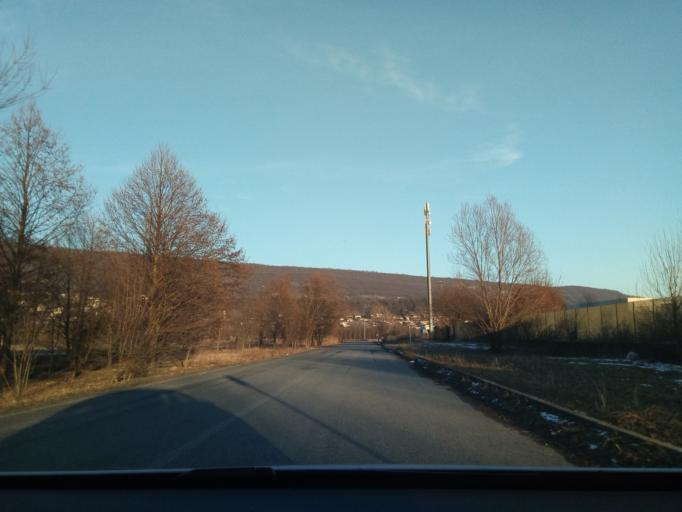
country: IT
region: Piedmont
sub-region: Provincia di Torino
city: Cascinette d'Ivrea
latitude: 45.4751
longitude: 7.9175
